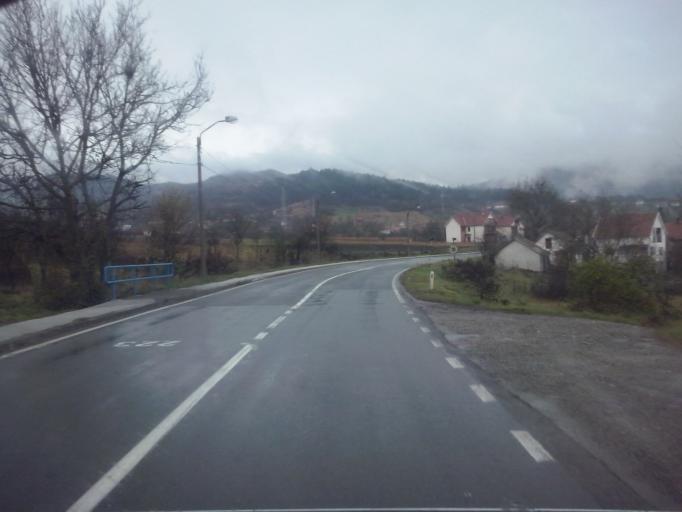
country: RS
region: Central Serbia
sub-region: Raski Okrug
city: Raska
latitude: 43.3802
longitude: 20.6280
